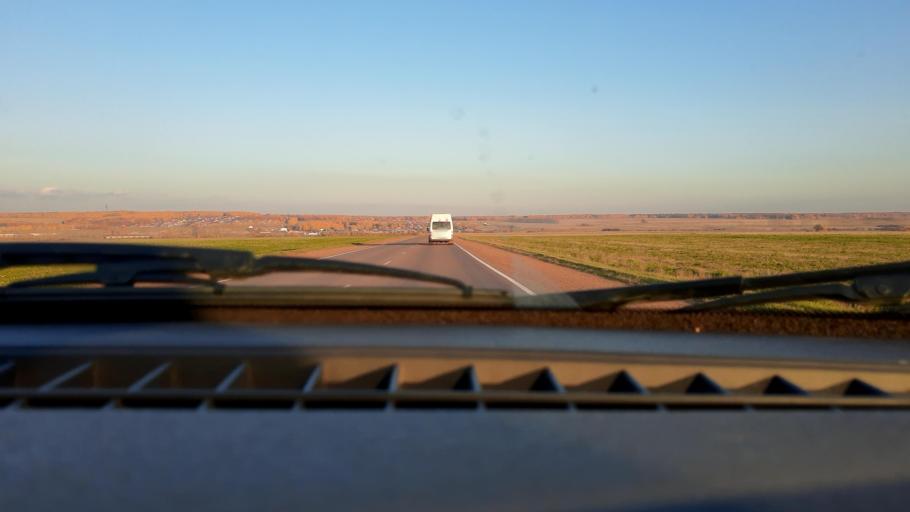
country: RU
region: Bashkortostan
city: Avdon
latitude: 54.8233
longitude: 55.6561
